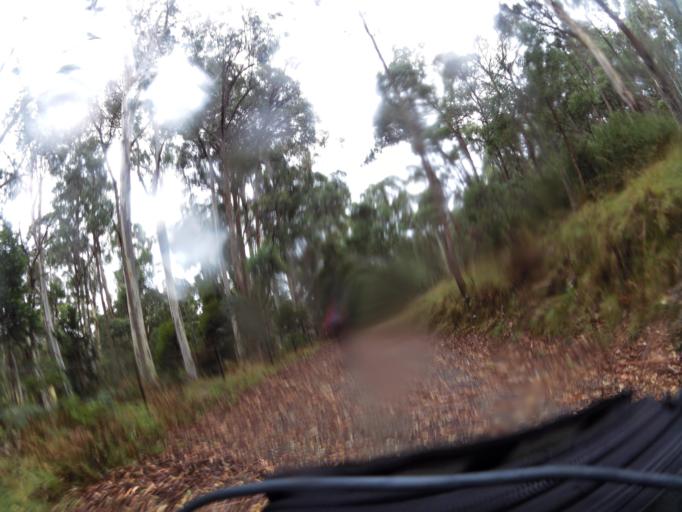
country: AU
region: New South Wales
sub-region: Greater Hume Shire
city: Holbrook
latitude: -36.1639
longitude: 147.4851
